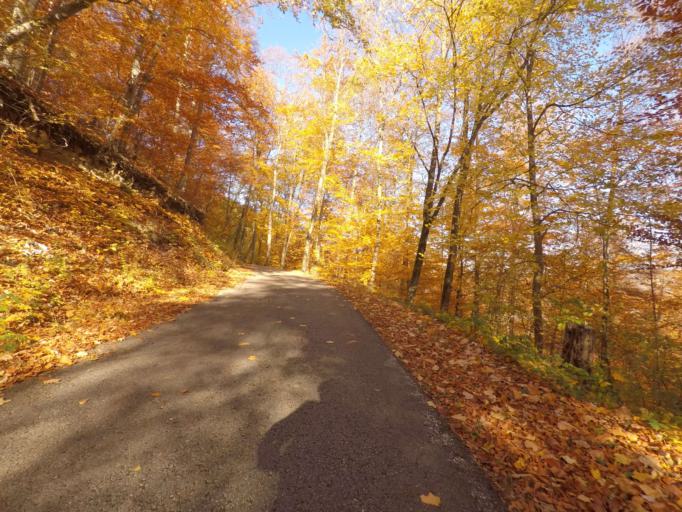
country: DE
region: Baden-Wuerttemberg
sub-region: Tuebingen Region
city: Pfullingen
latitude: 48.4396
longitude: 9.2328
